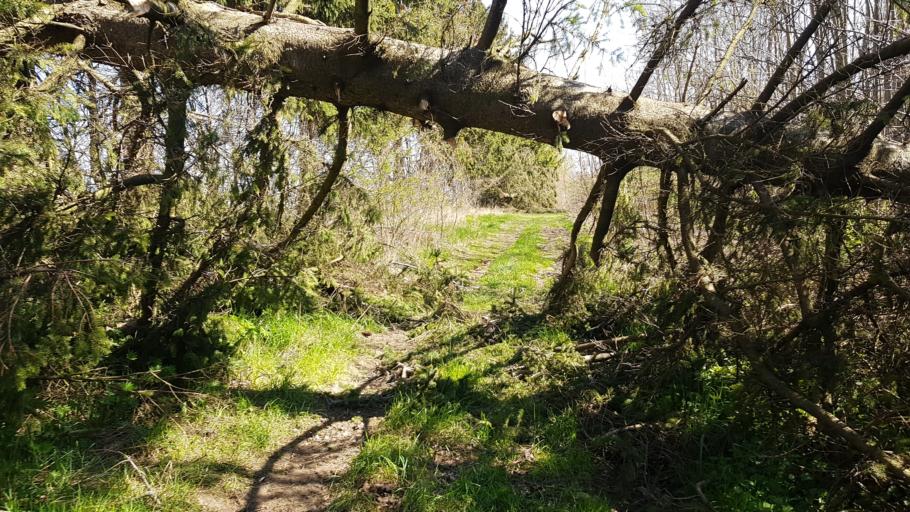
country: PL
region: Pomeranian Voivodeship
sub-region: Powiat slupski
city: Ustka
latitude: 54.5149
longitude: 16.7370
